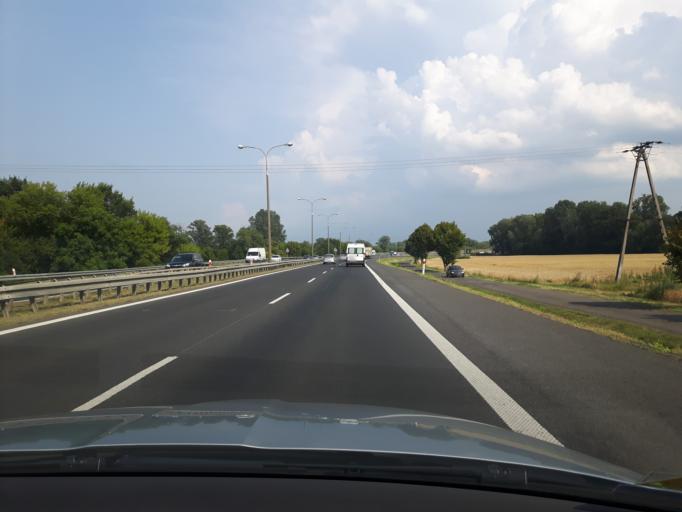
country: PL
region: Masovian Voivodeship
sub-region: Powiat nowodworski
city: Nowy Dwor Mazowiecki
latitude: 52.4151
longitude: 20.6875
